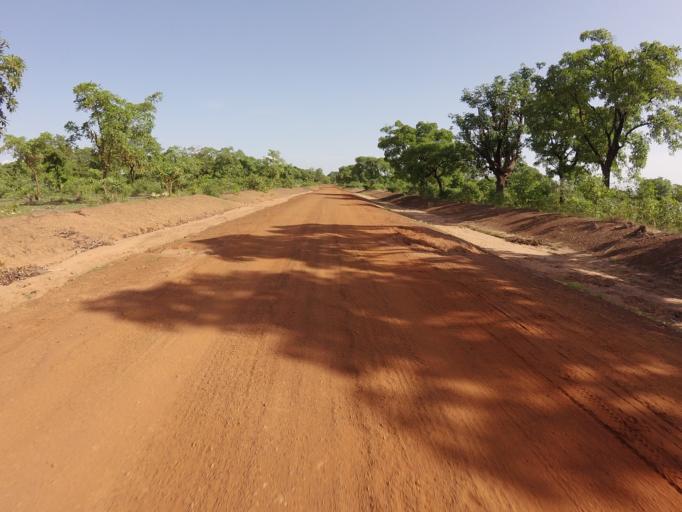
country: GH
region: Upper East
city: Bawku
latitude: 10.7432
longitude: -0.2004
